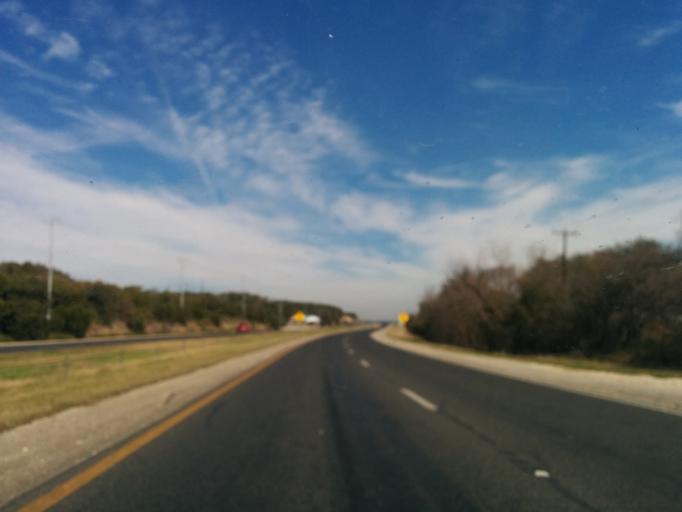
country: US
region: Texas
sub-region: Bexar County
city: Timberwood Park
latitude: 29.7069
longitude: -98.4501
